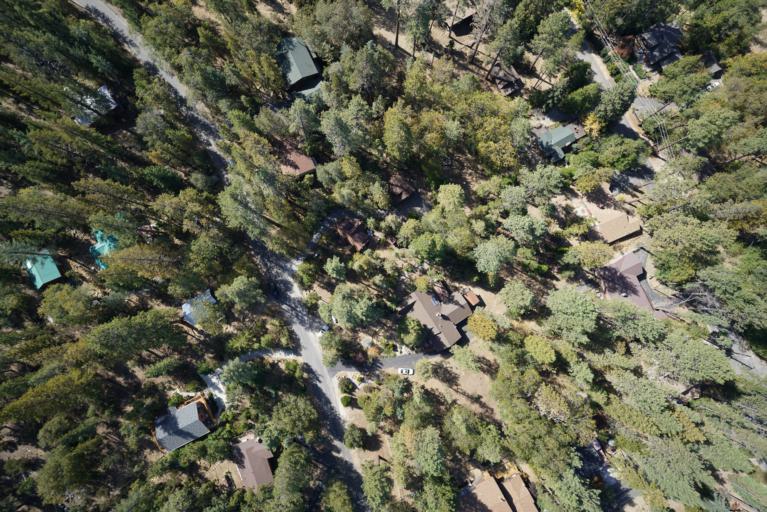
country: US
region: California
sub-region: Riverside County
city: Idyllwild
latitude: 33.7550
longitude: -116.6981
